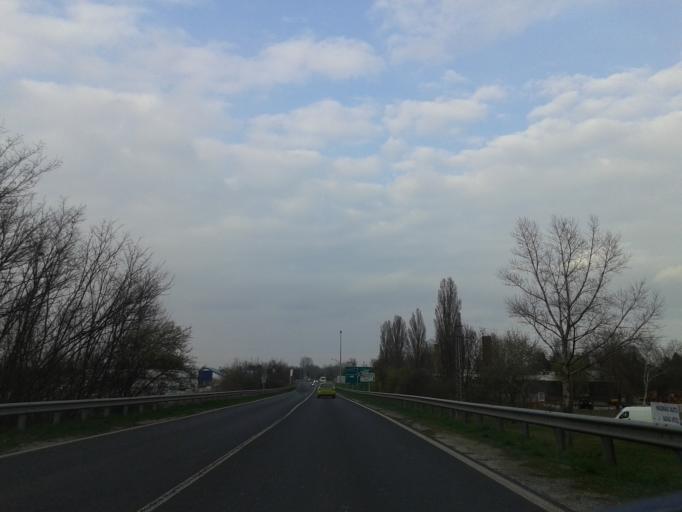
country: HU
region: Gyor-Moson-Sopron
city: Gyor
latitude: 47.7015
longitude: 17.6695
